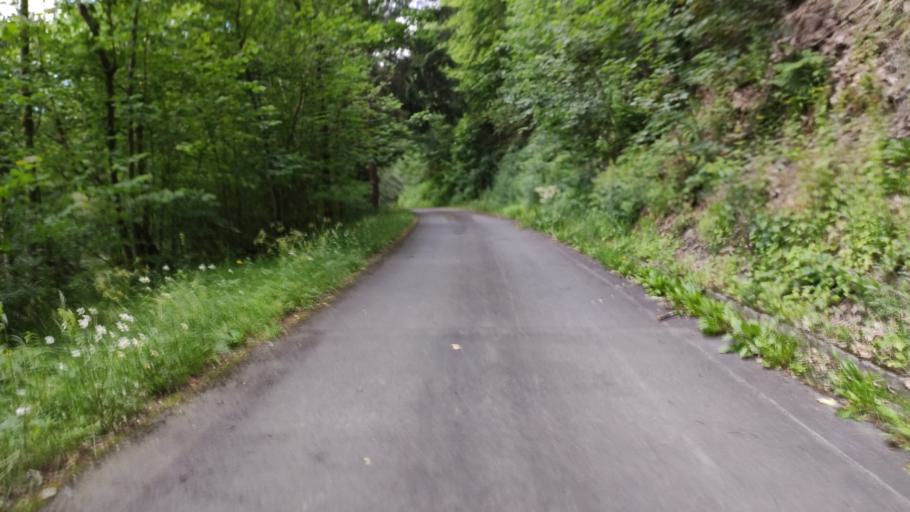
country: DE
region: Bavaria
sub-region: Upper Franconia
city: Nordhalben
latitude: 50.3588
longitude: 11.4879
